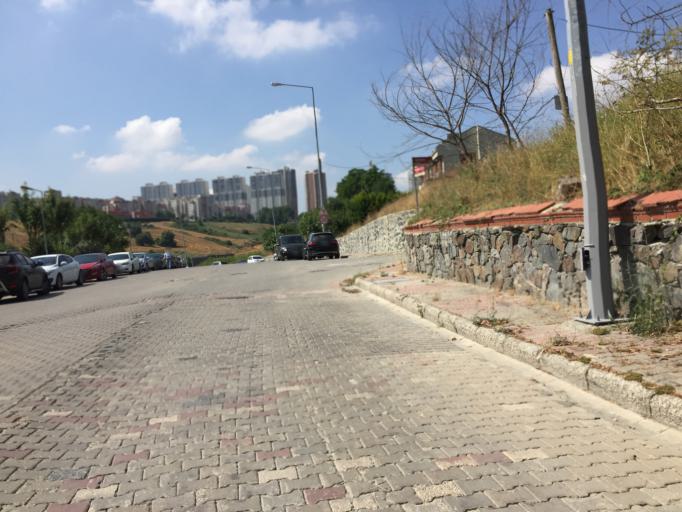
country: TR
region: Istanbul
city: Esenyurt
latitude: 41.0812
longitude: 28.6617
